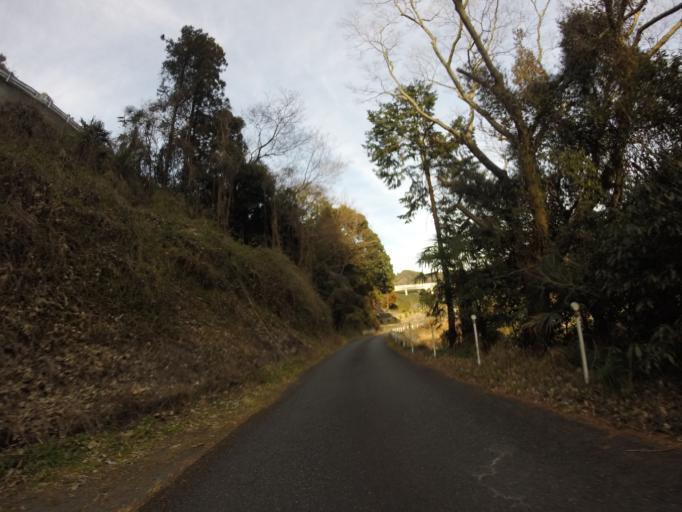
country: JP
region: Shizuoka
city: Shizuoka-shi
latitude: 35.0697
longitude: 138.4573
